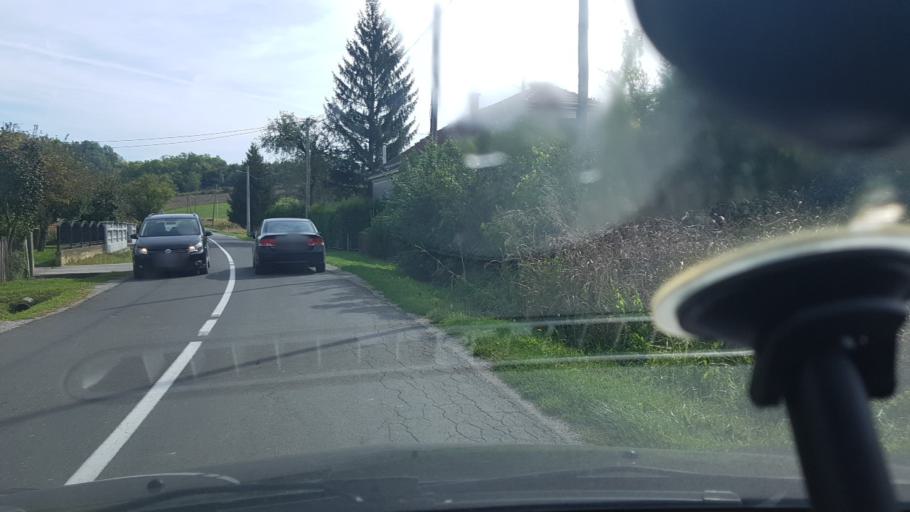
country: HR
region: Krapinsko-Zagorska
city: Zlatar
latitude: 46.1046
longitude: 16.2015
